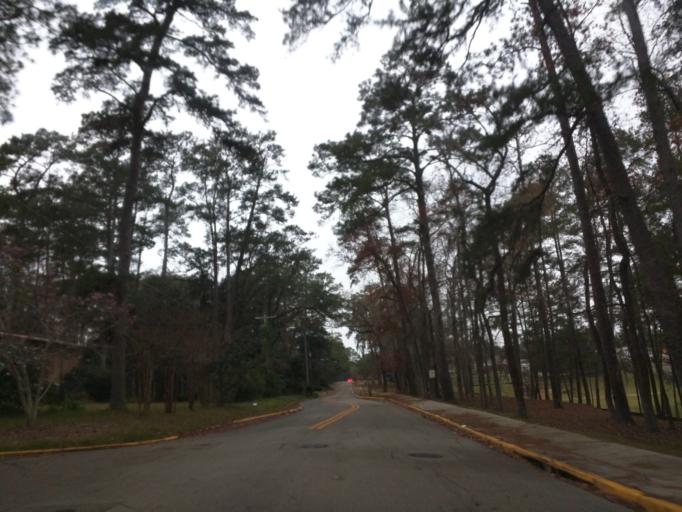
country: US
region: Florida
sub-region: Leon County
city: Tallahassee
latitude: 30.4509
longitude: -84.2651
